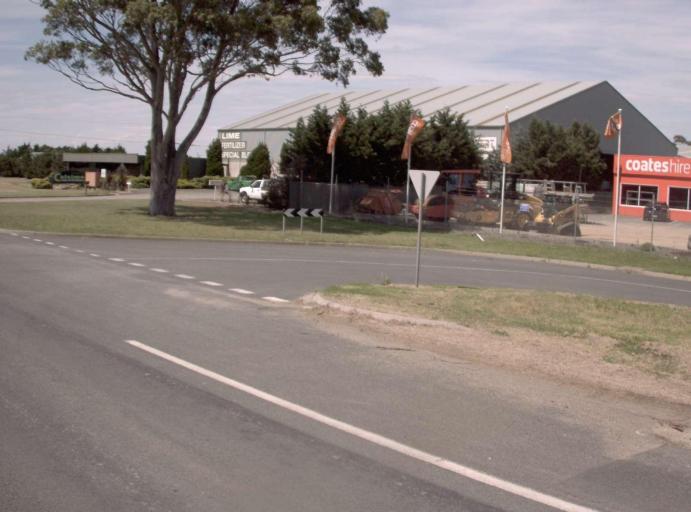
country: AU
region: Victoria
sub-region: Wellington
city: Sale
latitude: -38.0874
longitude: 147.0701
